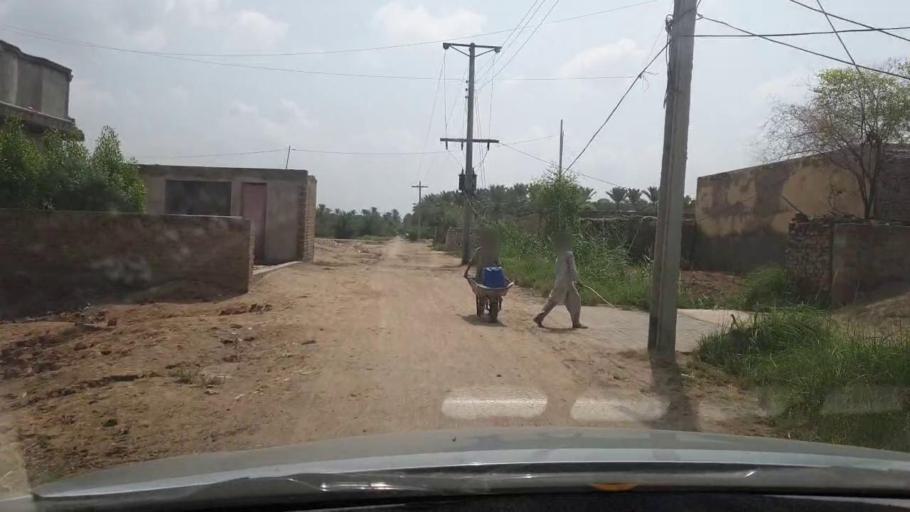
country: PK
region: Sindh
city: Khairpur
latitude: 27.5033
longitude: 68.7360
